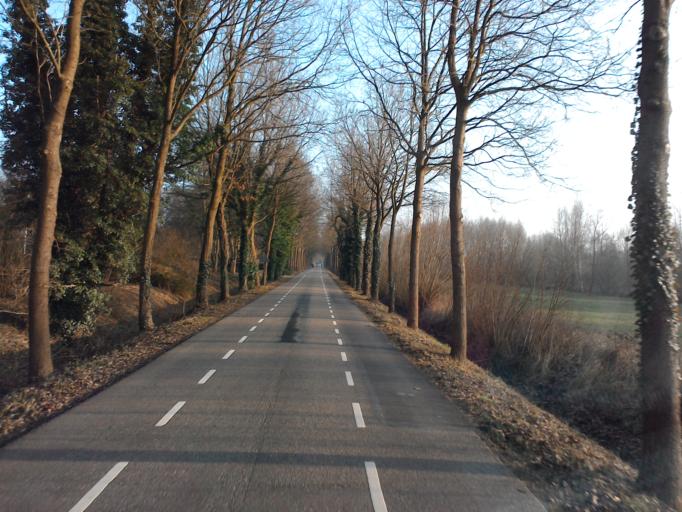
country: NL
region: Utrecht
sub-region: Gemeente Bunnik
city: Bunnik
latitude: 52.0730
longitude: 5.1981
